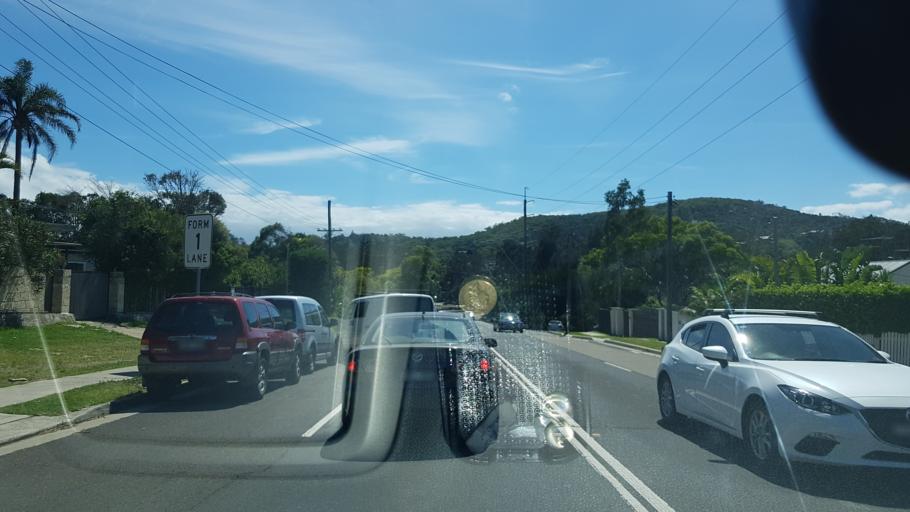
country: AU
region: New South Wales
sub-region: Pittwater
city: Bilgola Beach
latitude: -33.6287
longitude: 151.3315
